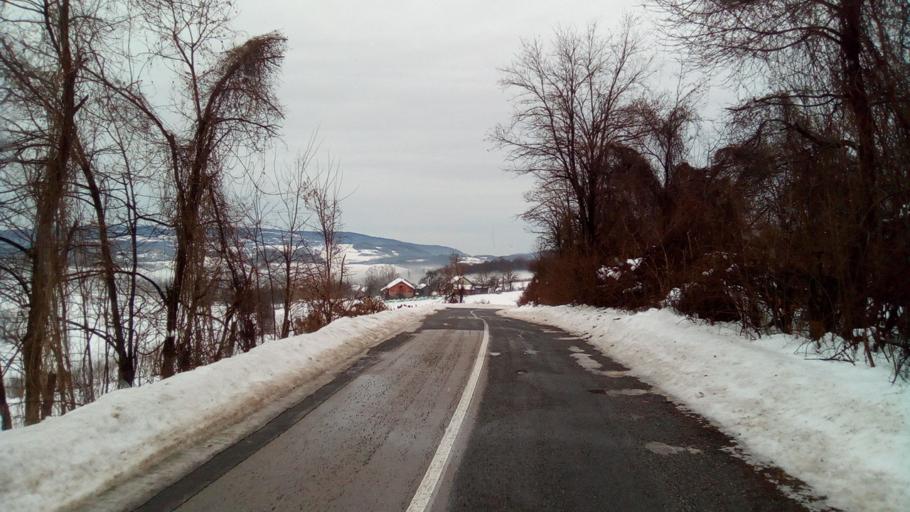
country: HR
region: Sisacko-Moslavacka
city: Petrinja
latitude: 45.3366
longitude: 16.2473
